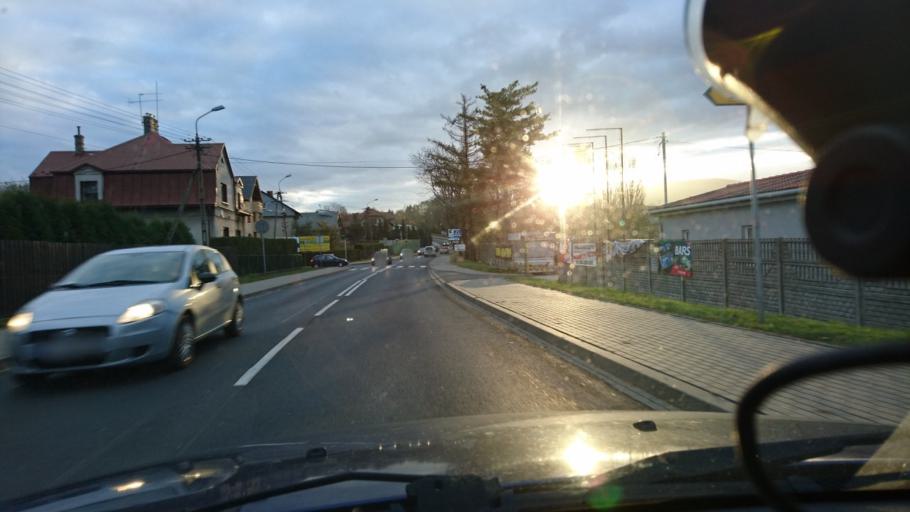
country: PL
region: Silesian Voivodeship
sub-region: Bielsko-Biala
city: Bielsko-Biala
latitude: 49.8408
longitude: 19.0549
